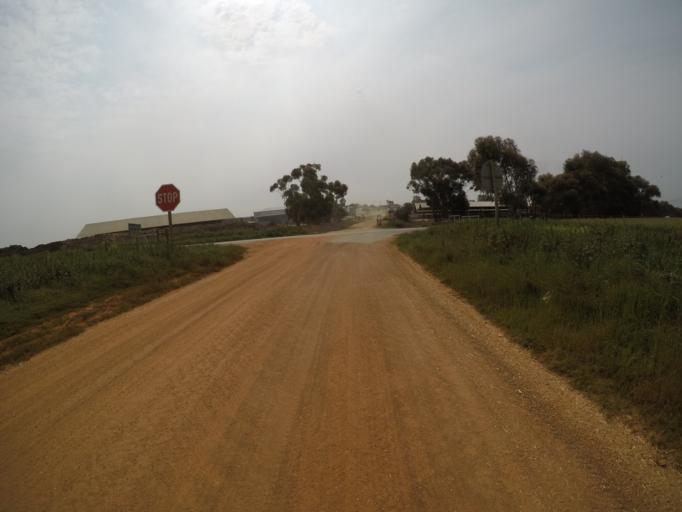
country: ZA
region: Western Cape
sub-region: City of Cape Town
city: Kraaifontein
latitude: -33.7069
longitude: 18.6909
